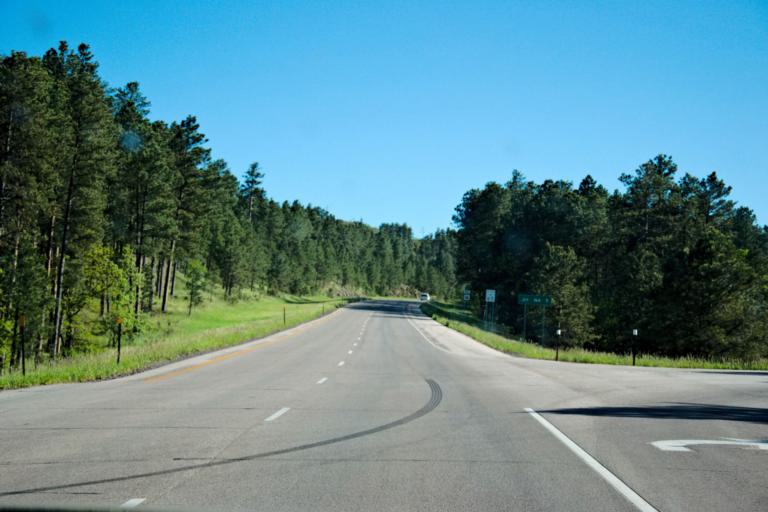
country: US
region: South Dakota
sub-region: Pennington County
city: Colonial Pine Hills
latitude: 43.9516
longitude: -103.3671
